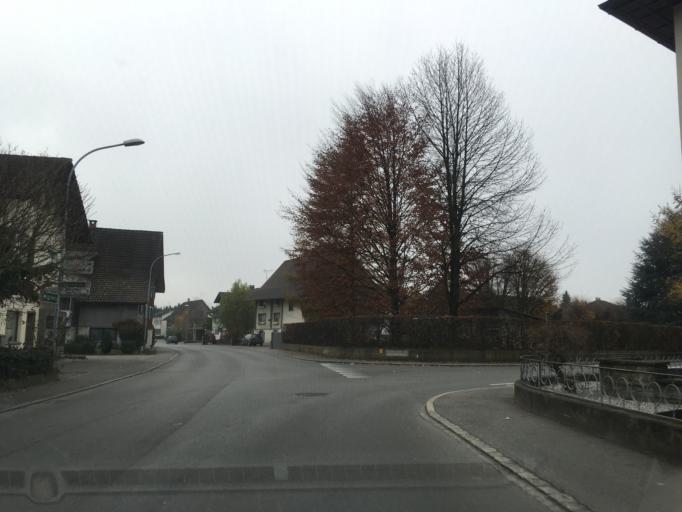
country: AT
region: Vorarlberg
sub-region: Politischer Bezirk Dornbirn
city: Lustenau
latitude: 47.4317
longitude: 9.6650
